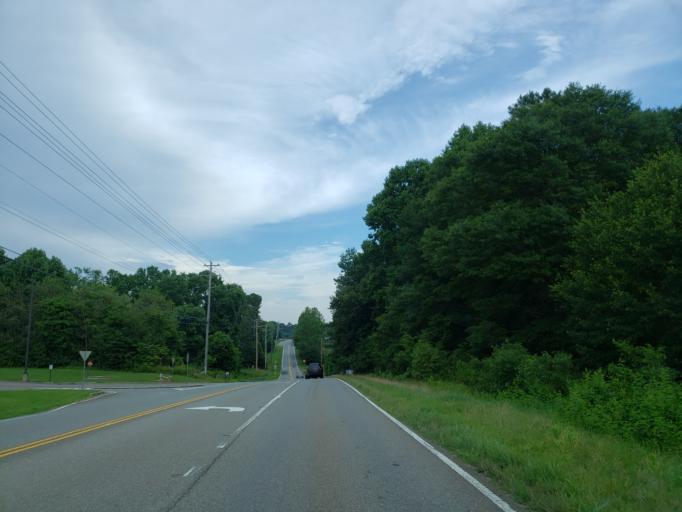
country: US
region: Georgia
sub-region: Cherokee County
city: Canton
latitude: 34.2134
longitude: -84.3938
